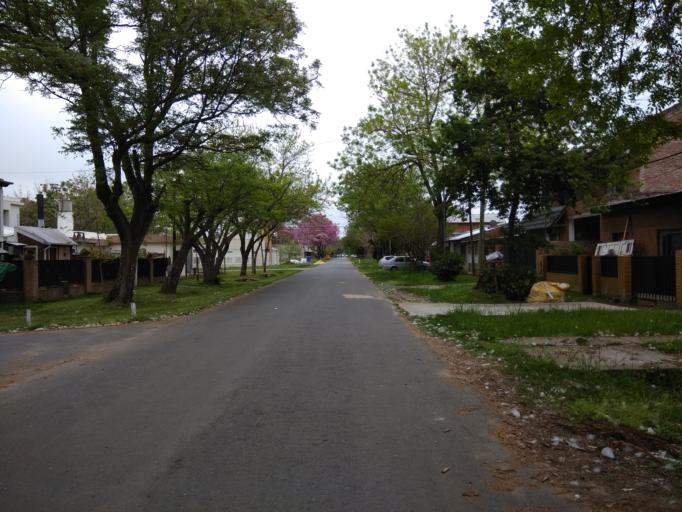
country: AR
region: Santa Fe
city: Granadero Baigorria
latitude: -32.8492
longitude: -60.6977
